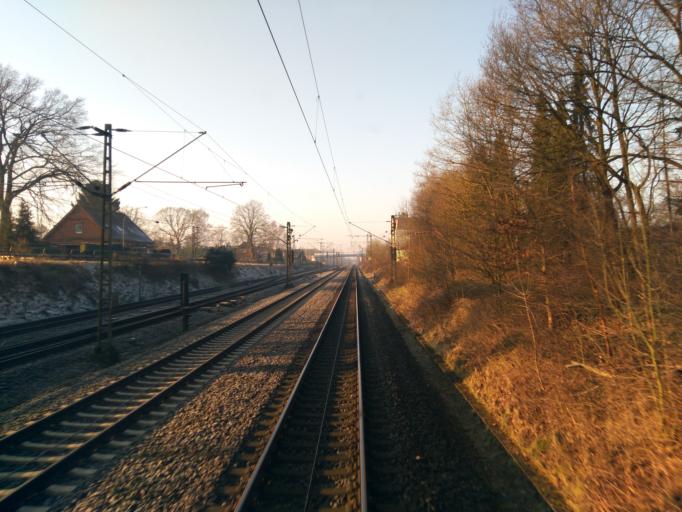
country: DE
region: Lower Saxony
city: Tostedt
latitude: 53.2767
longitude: 9.7420
